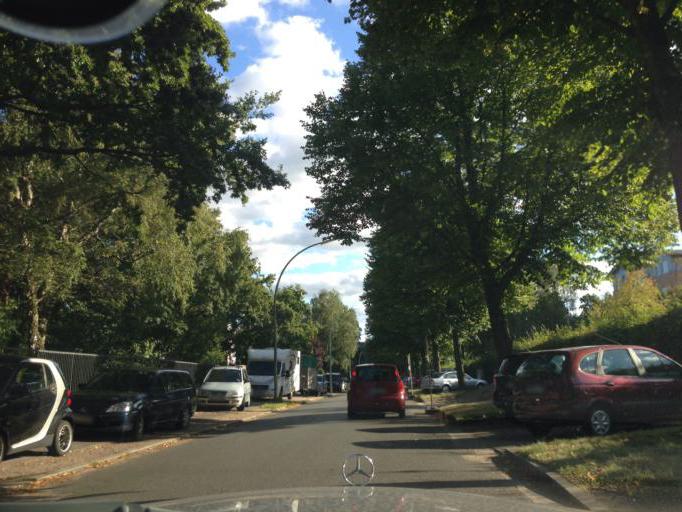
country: DE
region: Hamburg
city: Wandsbek
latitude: 53.5610
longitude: 10.0954
